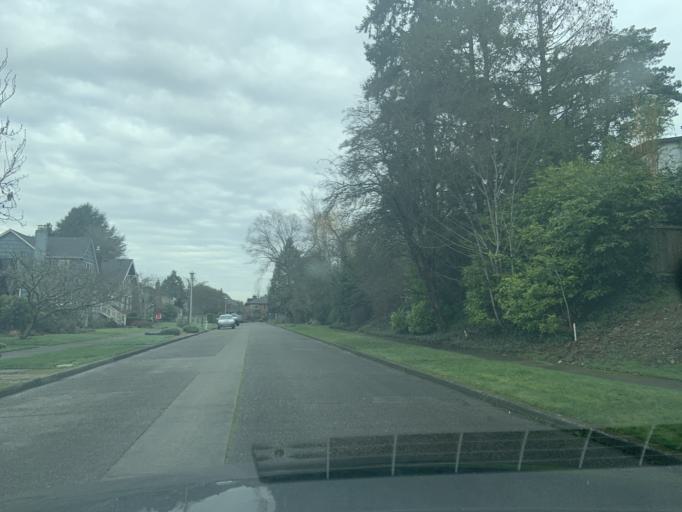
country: US
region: Washington
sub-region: King County
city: Yarrow Point
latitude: 47.6571
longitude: -122.2801
